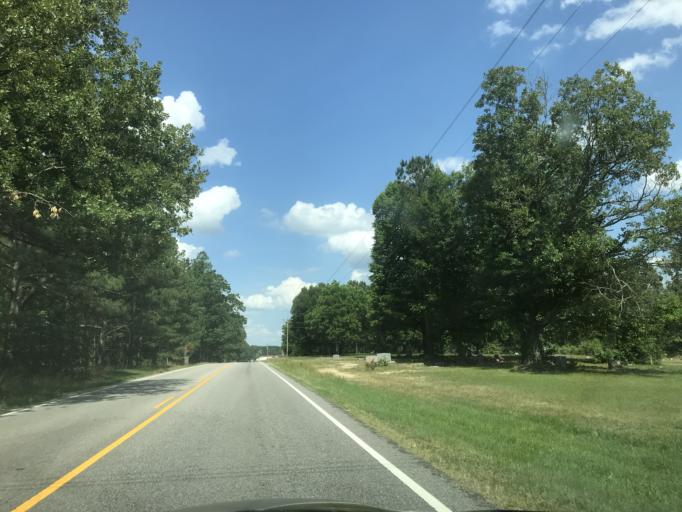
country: US
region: North Carolina
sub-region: Wake County
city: Rolesville
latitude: 35.9759
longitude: -78.3581
